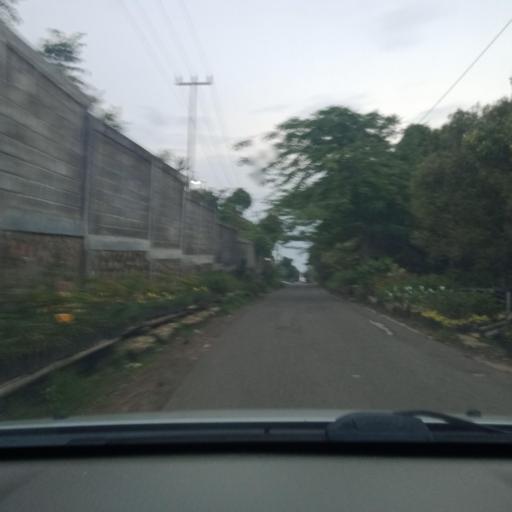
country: ID
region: West Java
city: Lembang
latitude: -6.8250
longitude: 107.5855
